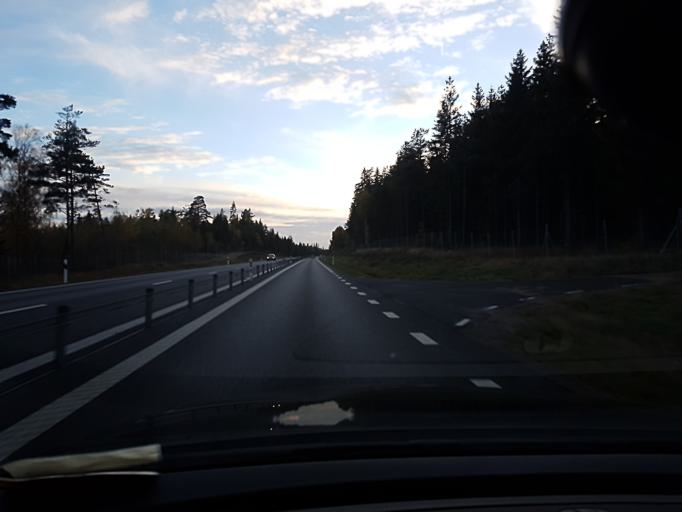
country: SE
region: Kronoberg
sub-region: Ljungby Kommun
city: Ljungby
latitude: 56.7701
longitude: 13.8035
